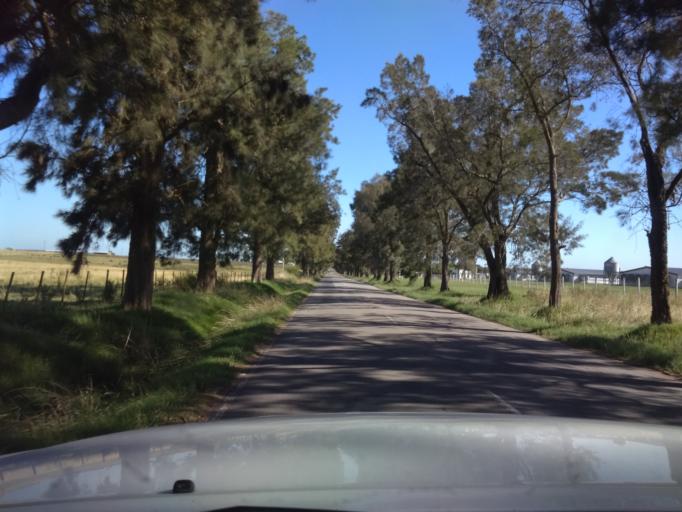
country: UY
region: Canelones
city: San Bautista
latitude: -34.3927
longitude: -55.9596
